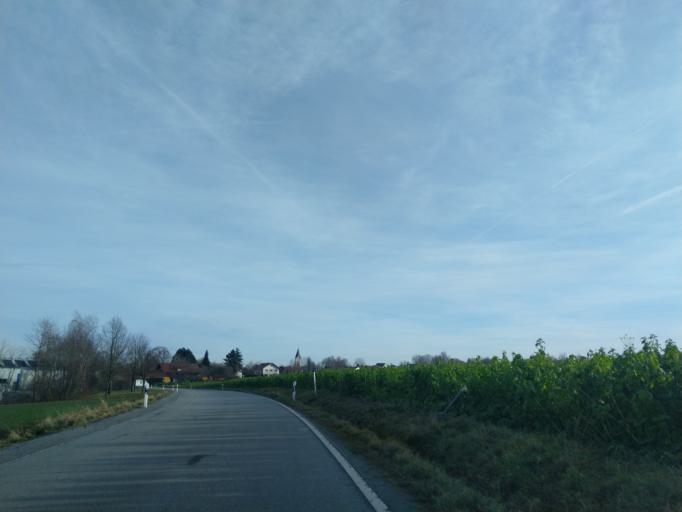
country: DE
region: Bavaria
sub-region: Lower Bavaria
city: Wallerfing
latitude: 48.6864
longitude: 12.8738
